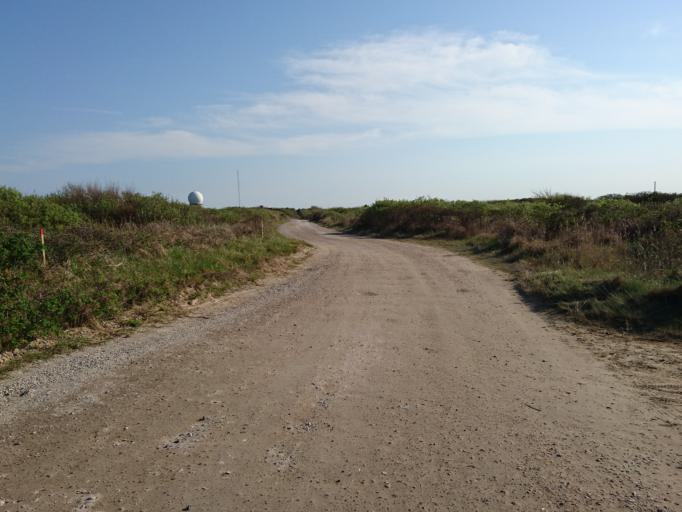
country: DK
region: North Denmark
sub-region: Frederikshavn Kommune
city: Skagen
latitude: 57.7501
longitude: 10.6041
